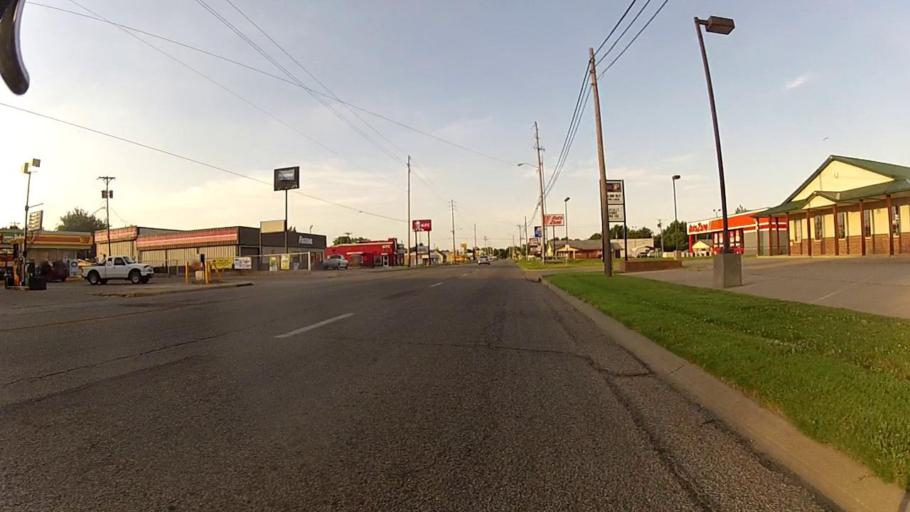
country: US
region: Kansas
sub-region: Cowley County
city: Arkansas City
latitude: 37.0830
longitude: -97.0402
